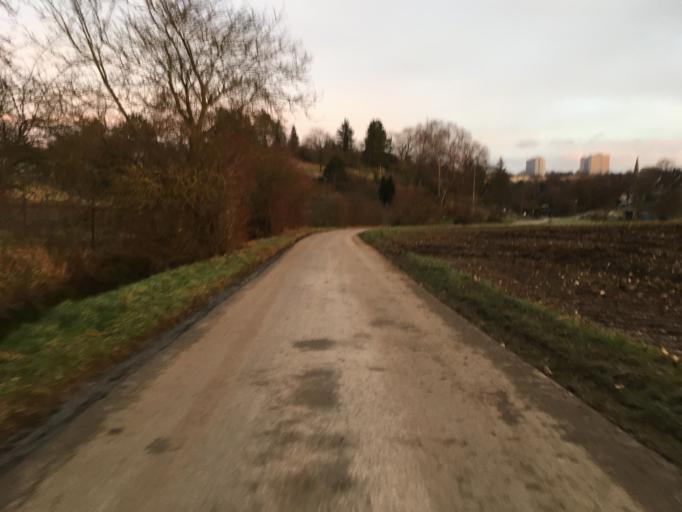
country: DE
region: Baden-Wuerttemberg
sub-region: Regierungsbezirk Stuttgart
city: Kornwestheim
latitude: 48.8451
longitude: 9.1930
